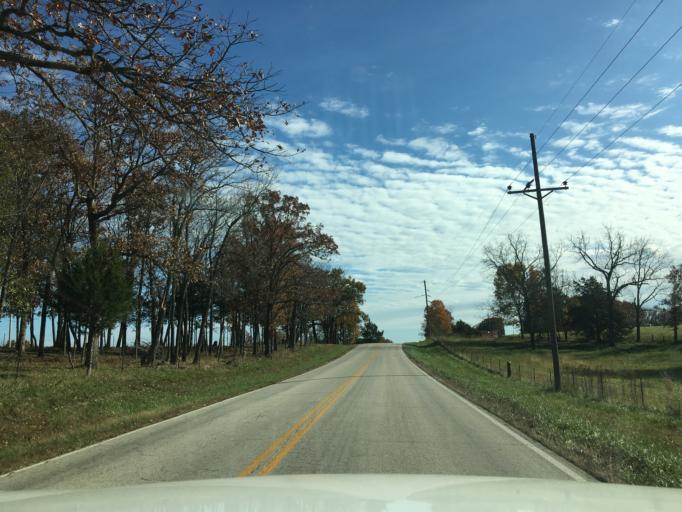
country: US
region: Missouri
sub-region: Osage County
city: Linn
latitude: 38.3744
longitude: -91.8140
